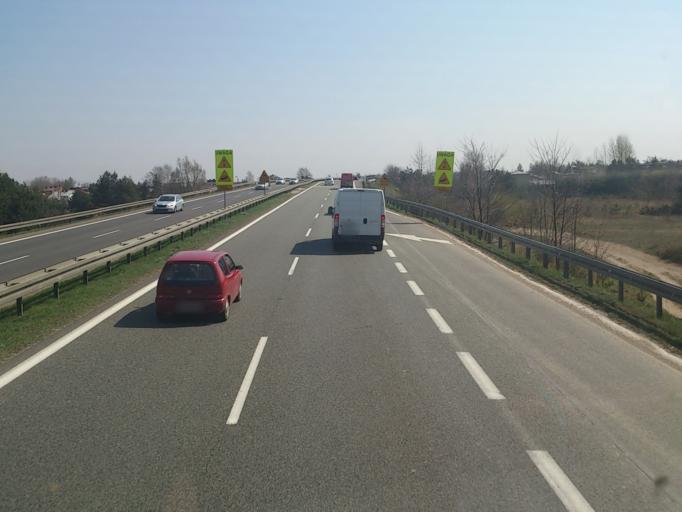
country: PL
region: Silesian Voivodeship
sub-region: Powiat bedzinski
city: Siewierz
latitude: 50.4791
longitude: 19.2260
